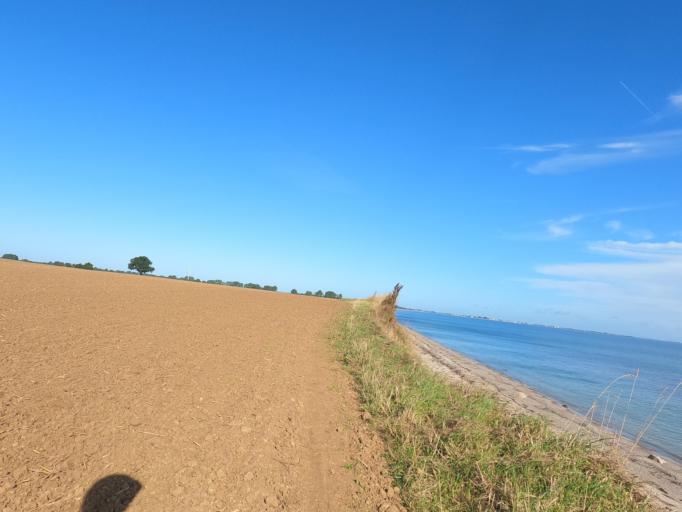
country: DE
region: Schleswig-Holstein
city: Neukirchen
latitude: 54.2898
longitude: 11.0803
